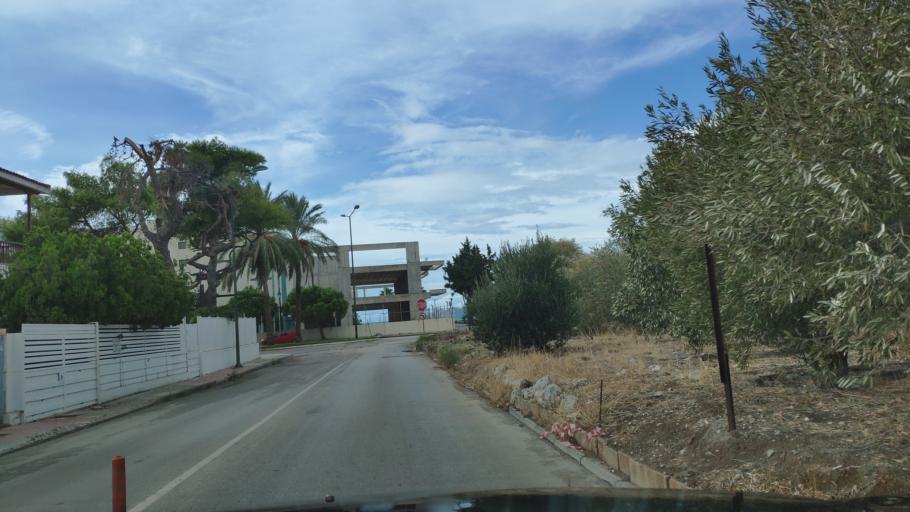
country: GR
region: Peloponnese
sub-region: Nomos Korinthias
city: Loutraki
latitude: 37.9615
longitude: 22.9708
